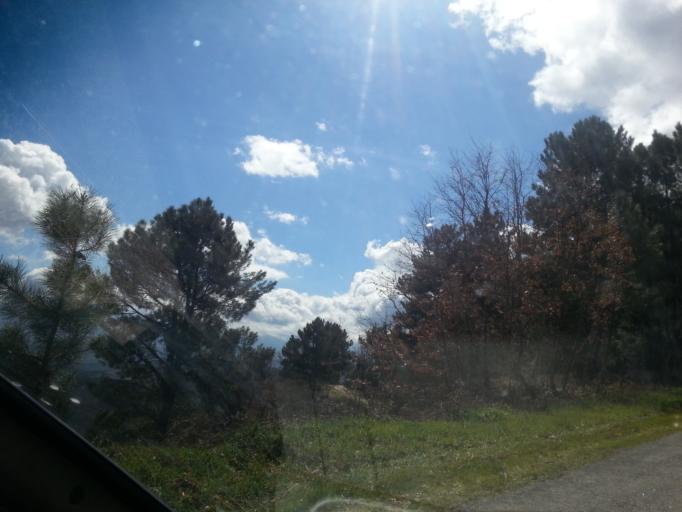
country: PT
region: Guarda
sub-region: Fornos de Algodres
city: Fornos de Algodres
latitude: 40.6562
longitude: -7.5068
